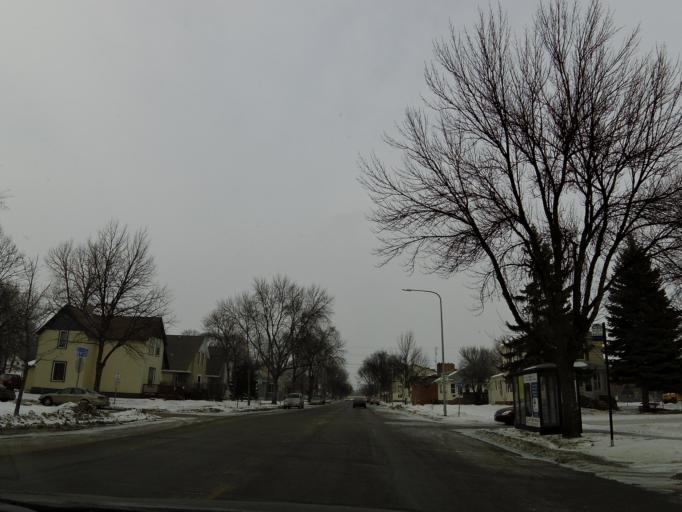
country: US
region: North Dakota
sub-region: Grand Forks County
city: Grand Forks
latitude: 47.9239
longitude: -97.0384
